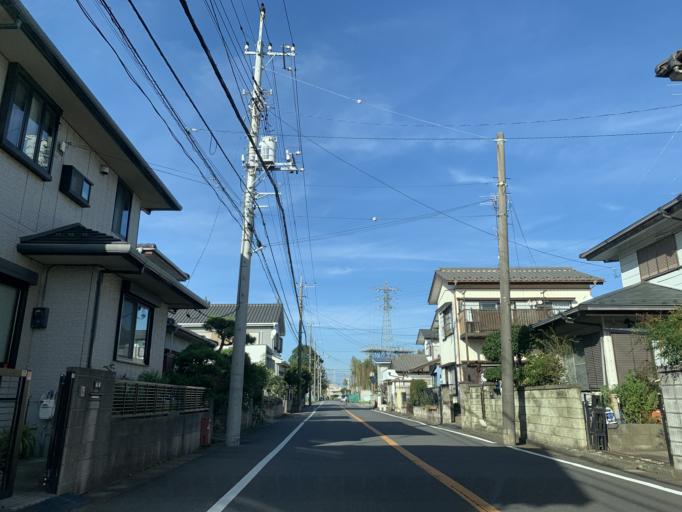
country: JP
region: Chiba
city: Nagareyama
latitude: 35.8970
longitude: 139.9291
